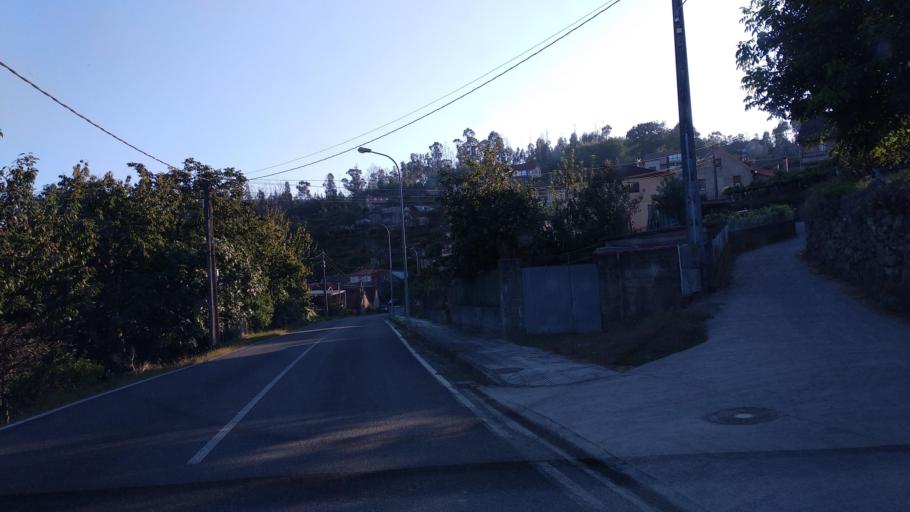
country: ES
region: Galicia
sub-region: Provincia de Pontevedra
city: Ponte Caldelas
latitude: 42.3526
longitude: -8.5434
